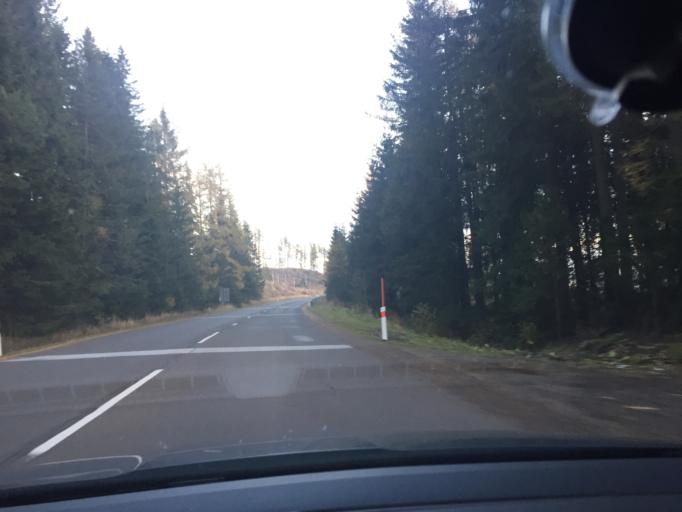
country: SK
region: Presovsky
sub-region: Okres Poprad
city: Strba
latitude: 49.1168
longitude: 20.0864
